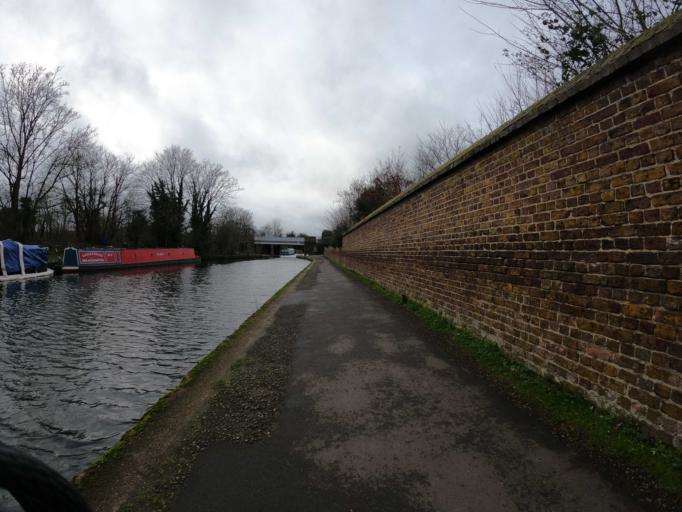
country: GB
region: England
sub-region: Greater London
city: Southall
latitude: 51.5048
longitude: -0.3544
